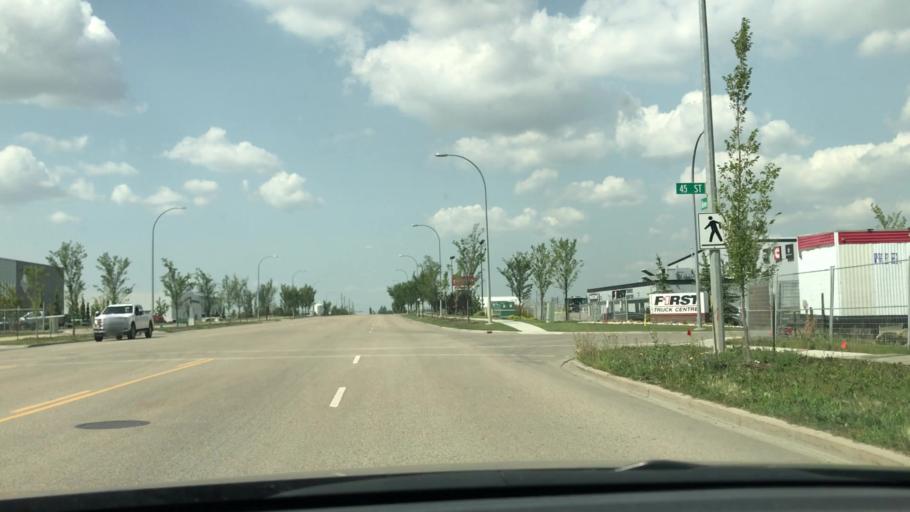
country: CA
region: Alberta
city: Edmonton
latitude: 53.4955
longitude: -113.4091
